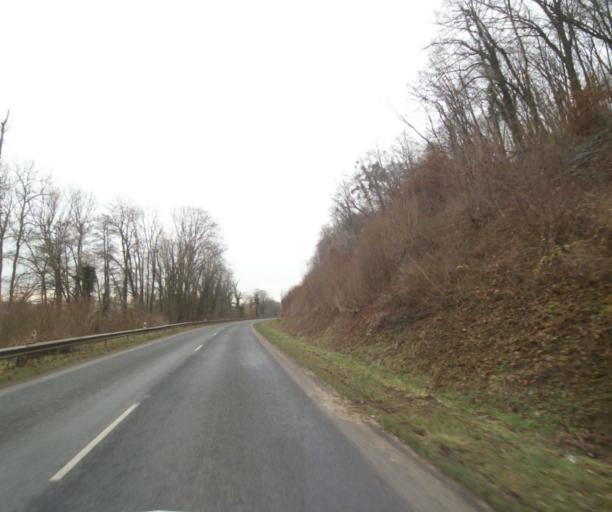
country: FR
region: Champagne-Ardenne
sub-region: Departement de la Haute-Marne
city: Bienville
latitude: 48.5561
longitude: 5.0650
